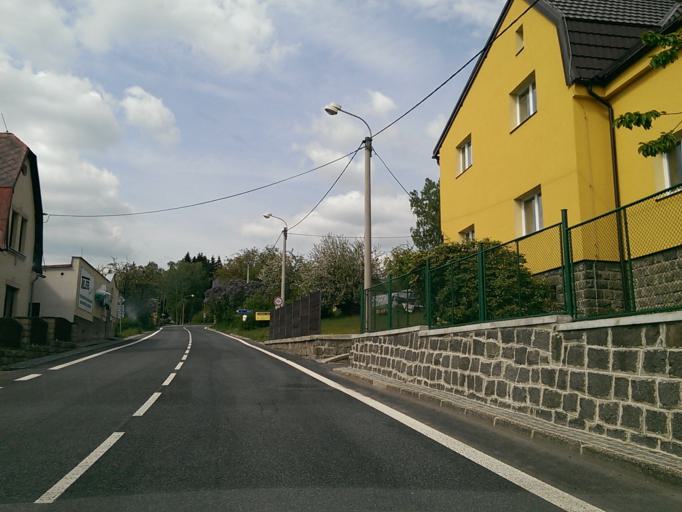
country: CZ
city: Pencin
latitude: 50.6830
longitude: 15.2693
